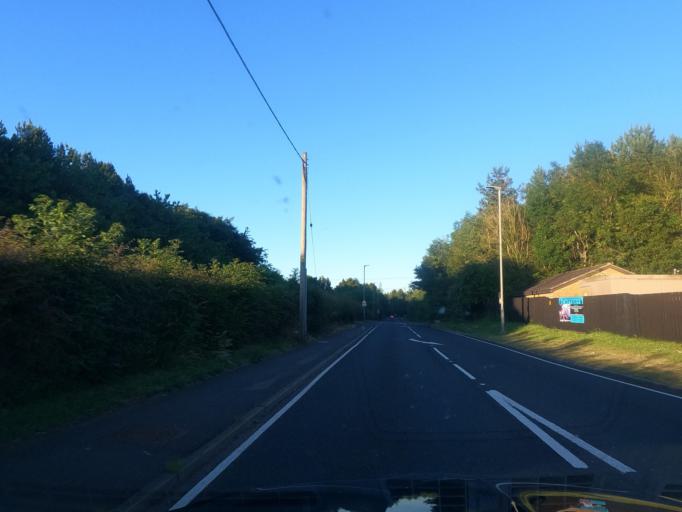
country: GB
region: England
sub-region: Northumberland
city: Seghill
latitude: 55.0794
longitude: -1.5536
